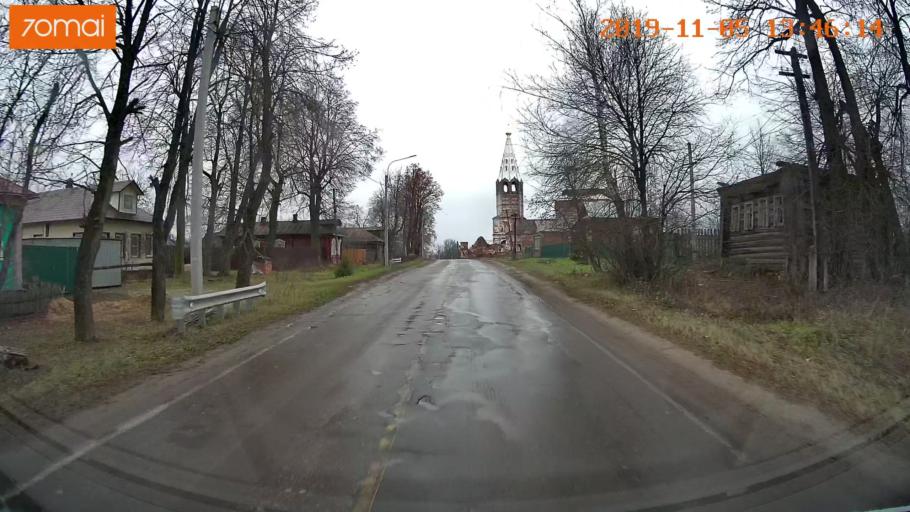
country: RU
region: Ivanovo
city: Shuya
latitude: 56.9943
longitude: 41.4101
